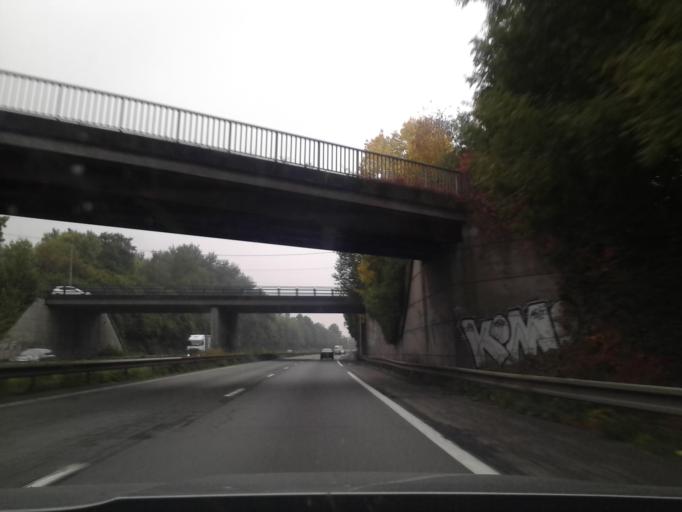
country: FR
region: Nord-Pas-de-Calais
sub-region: Departement du Nord
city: Saultain
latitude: 50.3414
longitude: 3.5670
